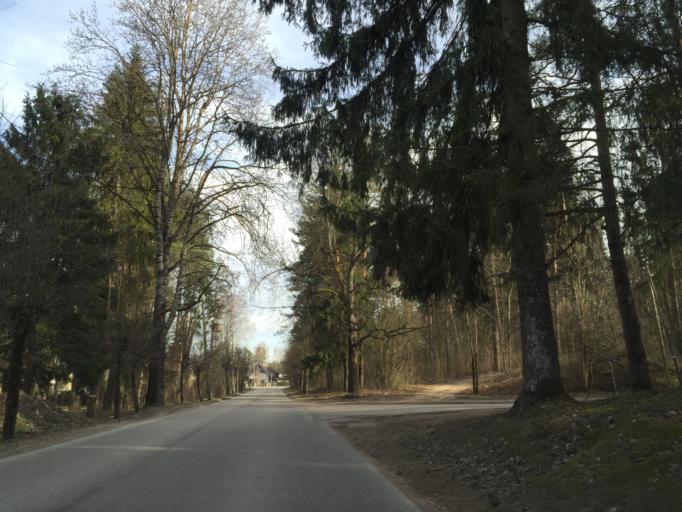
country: LV
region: Ogre
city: Ogre
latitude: 56.8134
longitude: 24.6228
